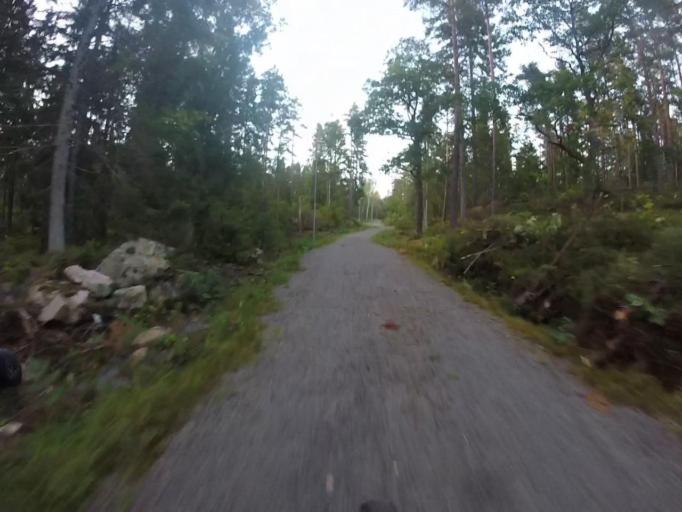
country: SE
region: Vaestra Goetaland
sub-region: Trollhattan
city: Trollhattan
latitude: 58.2956
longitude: 12.2694
